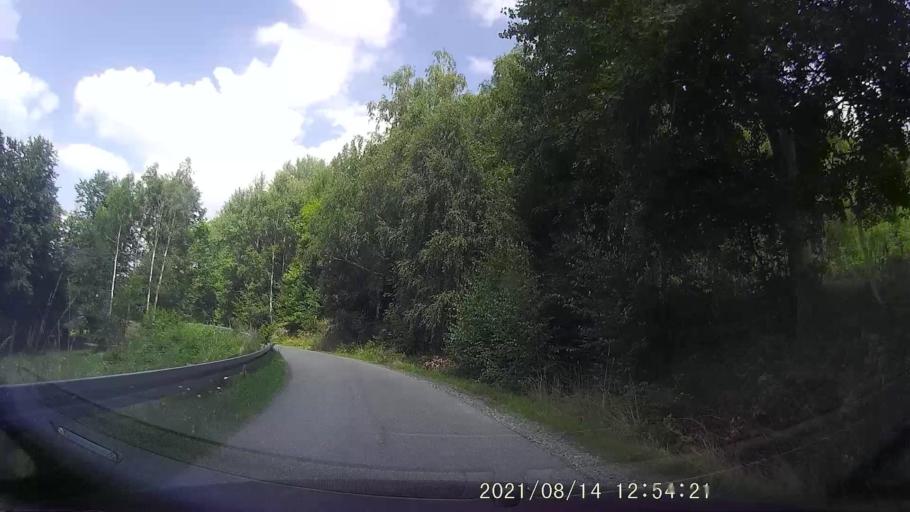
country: PL
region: Lower Silesian Voivodeship
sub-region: Powiat klodzki
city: Ladek-Zdroj
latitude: 50.3262
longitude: 16.8251
